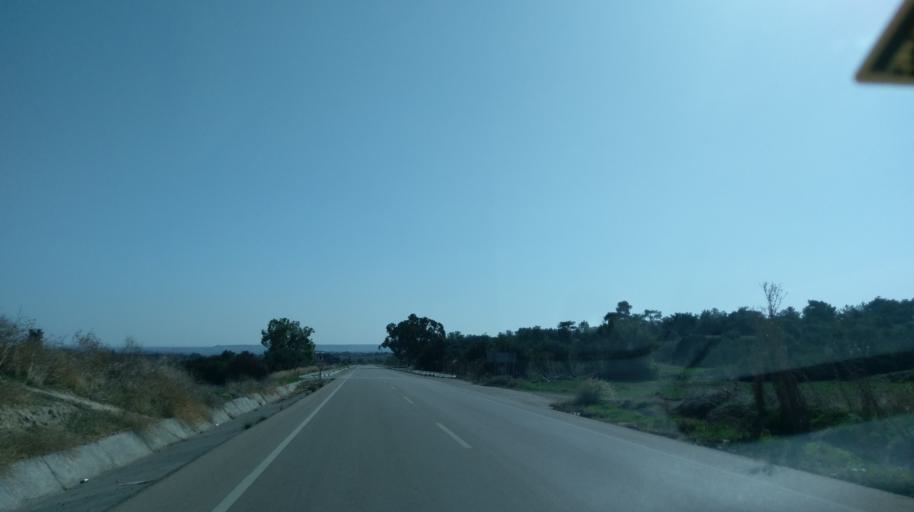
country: CY
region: Ammochostos
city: Trikomo
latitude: 35.4088
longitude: 33.9895
